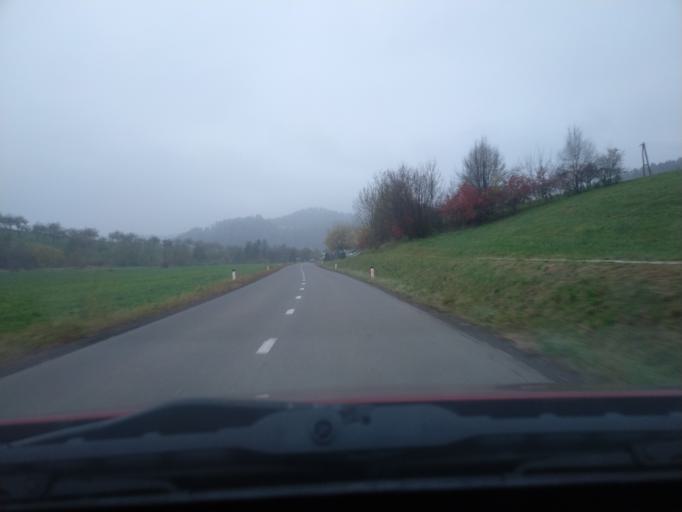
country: SI
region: Kungota
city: Zgornja Kungota
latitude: 46.6449
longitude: 15.6134
